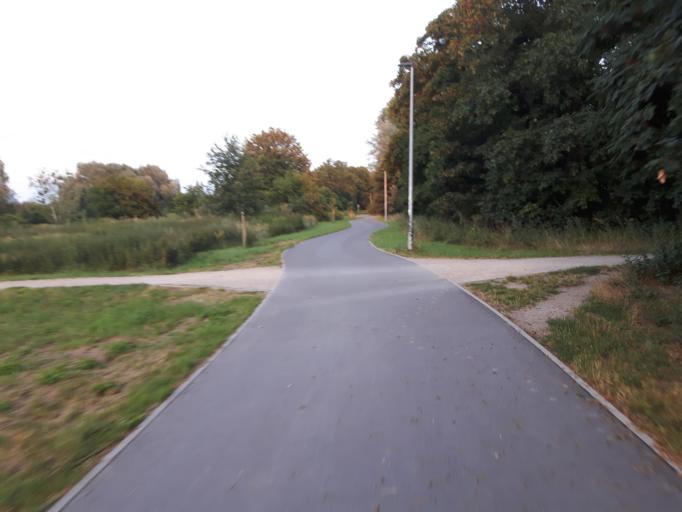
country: DE
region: Berlin
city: Staaken
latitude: 52.5567
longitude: 13.1281
